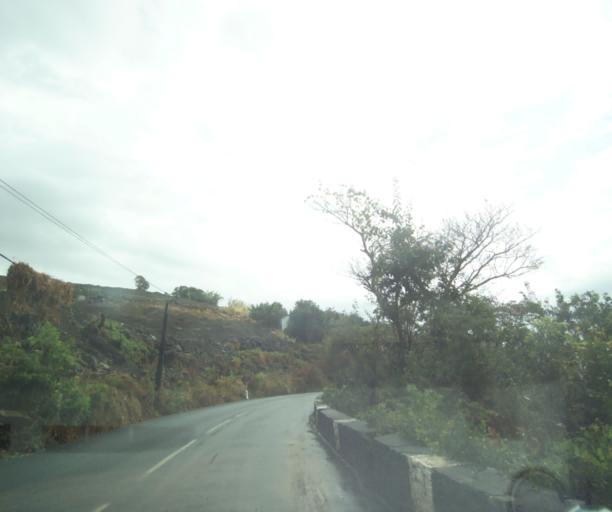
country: RE
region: Reunion
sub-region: Reunion
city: Saint-Paul
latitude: -21.0110
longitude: 55.3138
